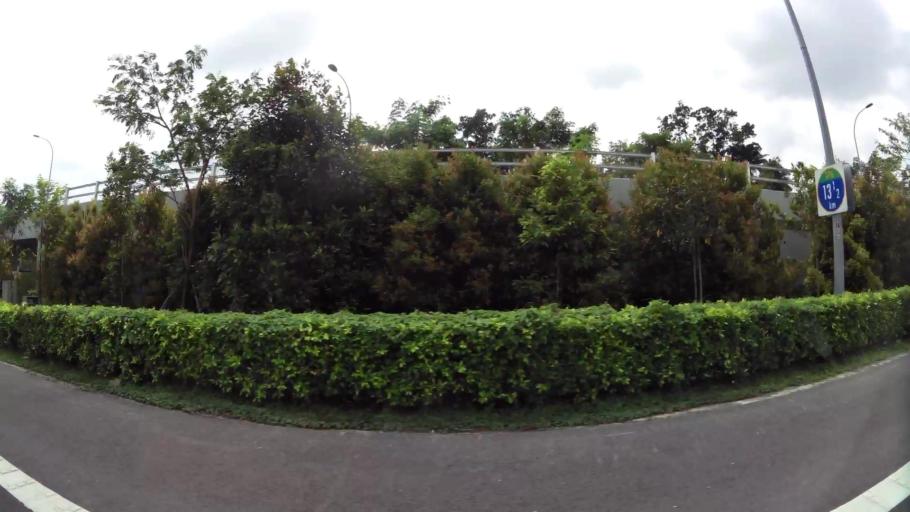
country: MY
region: Johor
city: Kampung Pasir Gudang Baru
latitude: 1.4008
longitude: 103.8656
